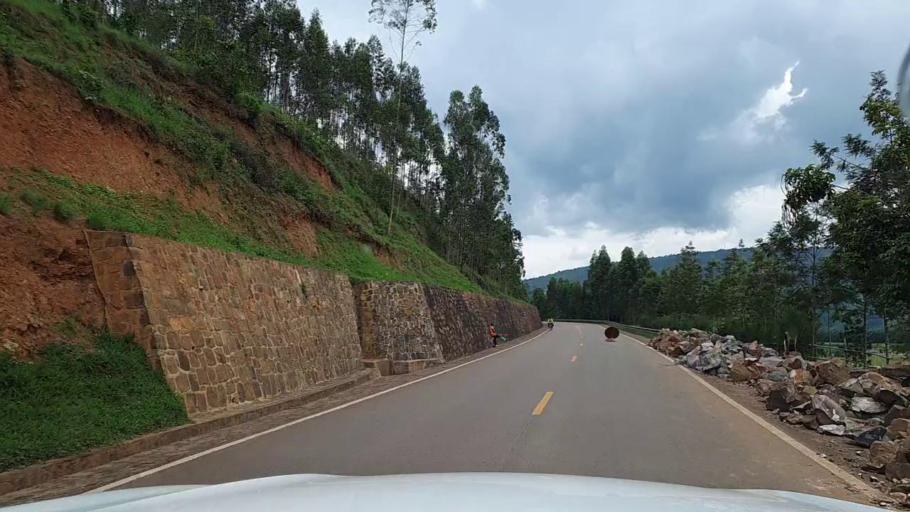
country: RW
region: Kigali
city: Kigali
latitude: -1.7907
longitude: 30.1284
